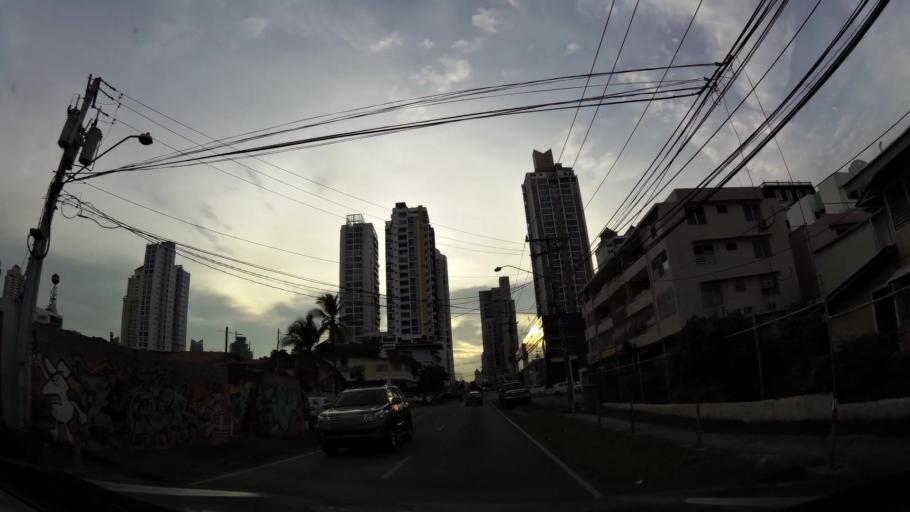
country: PA
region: Panama
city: Panama
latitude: 8.9940
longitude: -79.5098
